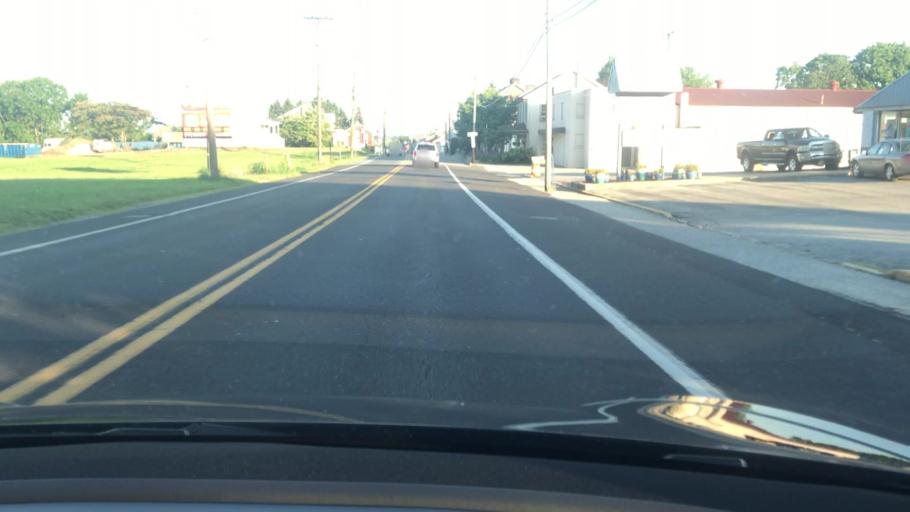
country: US
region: Pennsylvania
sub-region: York County
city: Dover
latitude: 40.0059
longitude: -76.8553
